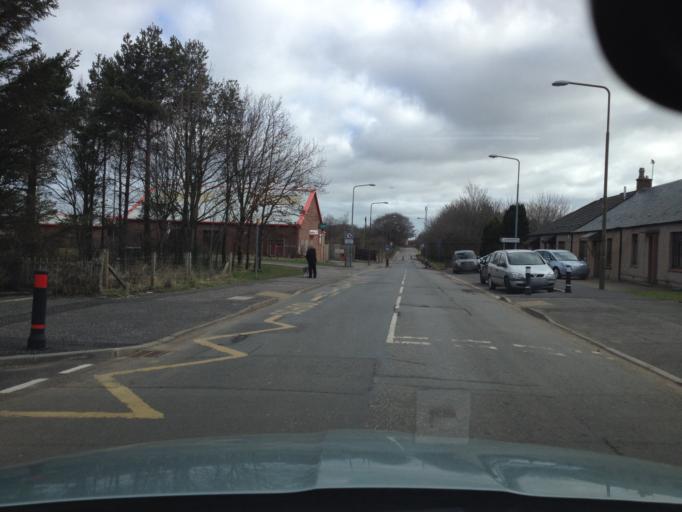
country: GB
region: Scotland
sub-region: West Lothian
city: Mid Calder
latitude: 55.9089
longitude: -3.4912
